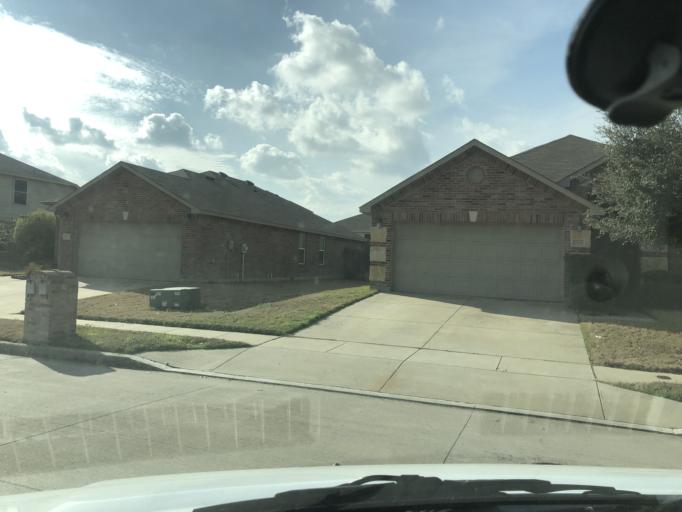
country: US
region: Texas
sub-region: Tarrant County
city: Saginaw
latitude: 32.9158
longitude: -97.3670
